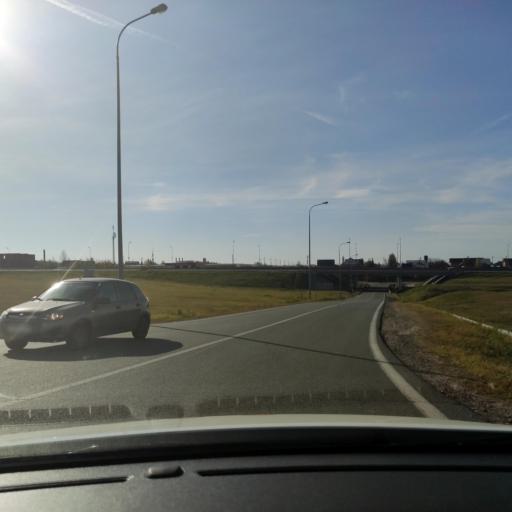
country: RU
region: Tatarstan
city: Vysokaya Gora
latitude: 55.7461
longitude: 49.4007
